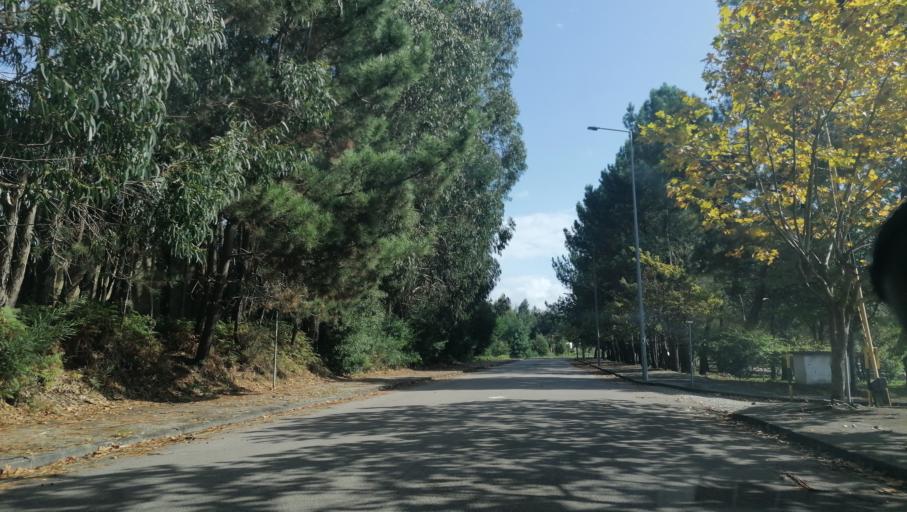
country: PT
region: Aveiro
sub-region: Espinho
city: Silvalde
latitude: 41.0008
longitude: -8.6225
